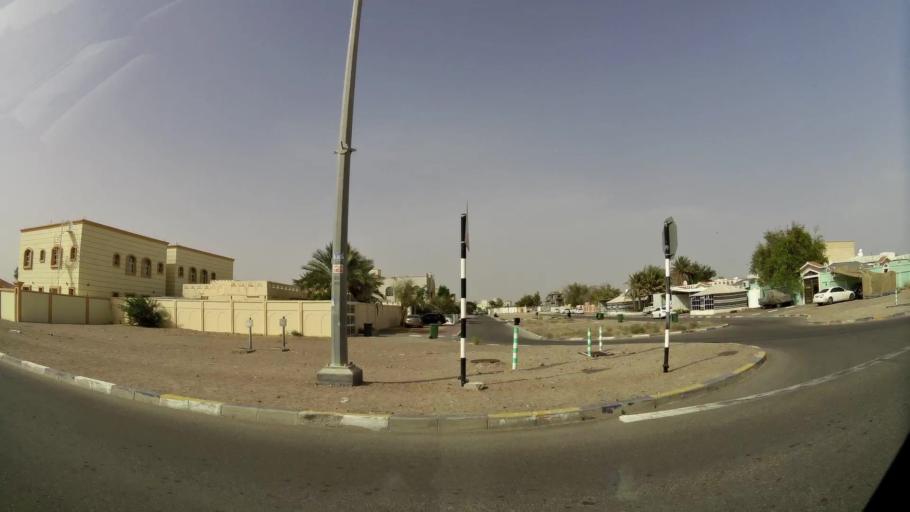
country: AE
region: Abu Dhabi
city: Al Ain
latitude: 24.2123
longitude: 55.5846
